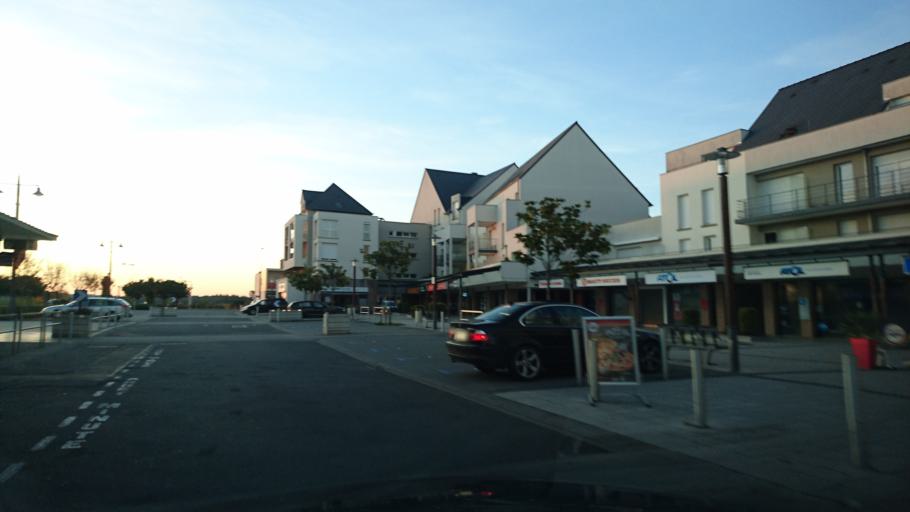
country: FR
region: Brittany
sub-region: Departement d'Ille-et-Vilaine
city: Bruz
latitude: 48.0297
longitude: -1.7587
